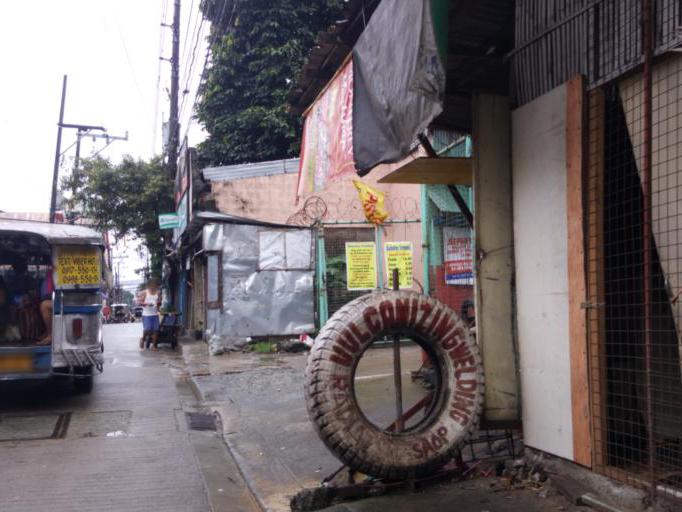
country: PH
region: Calabarzon
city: Bagong Pagasa
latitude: 14.7210
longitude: 121.0413
